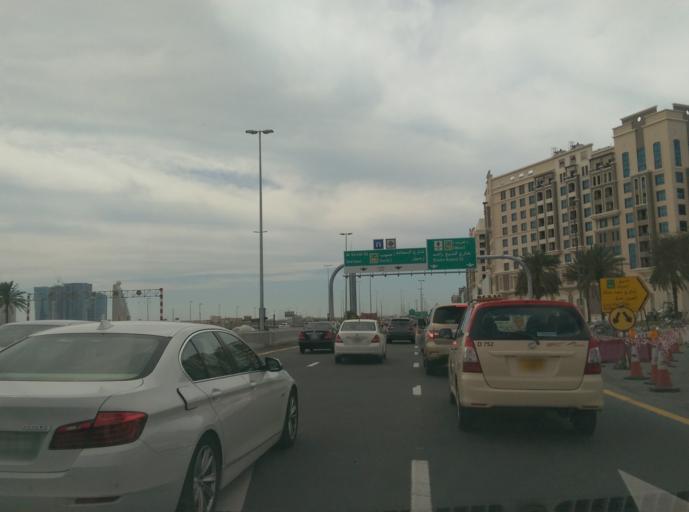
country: AE
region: Ash Shariqah
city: Sharjah
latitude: 25.2300
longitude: 55.3150
